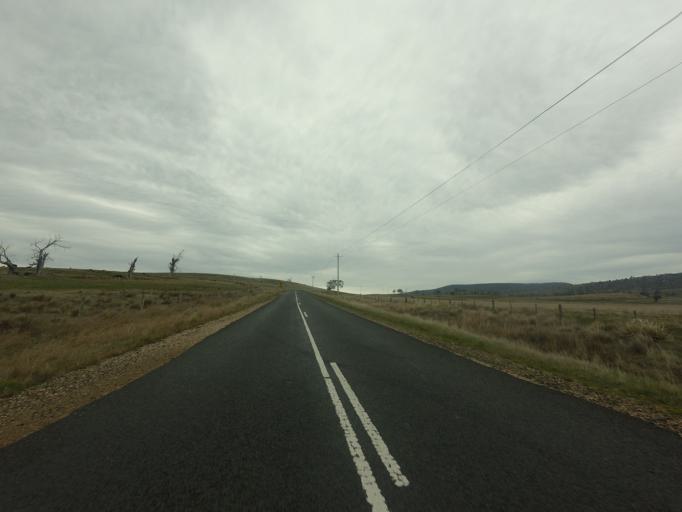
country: AU
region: Tasmania
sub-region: Derwent Valley
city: New Norfolk
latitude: -42.4289
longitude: 146.9896
